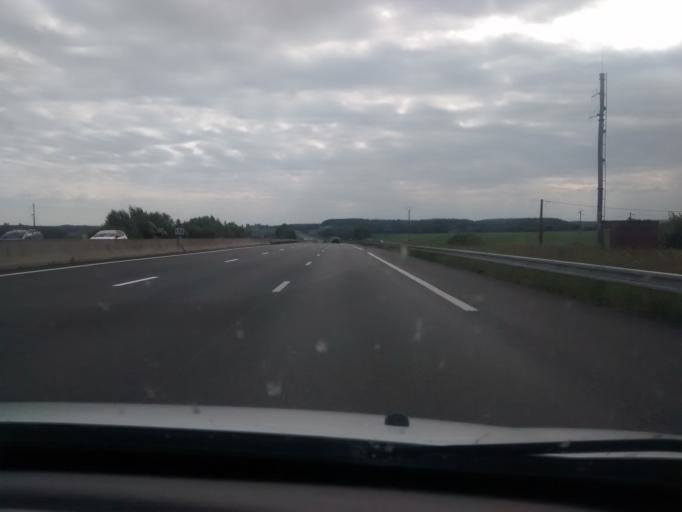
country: FR
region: Pays de la Loire
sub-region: Departement de la Sarthe
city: Cherre
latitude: 48.1448
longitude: 0.6720
